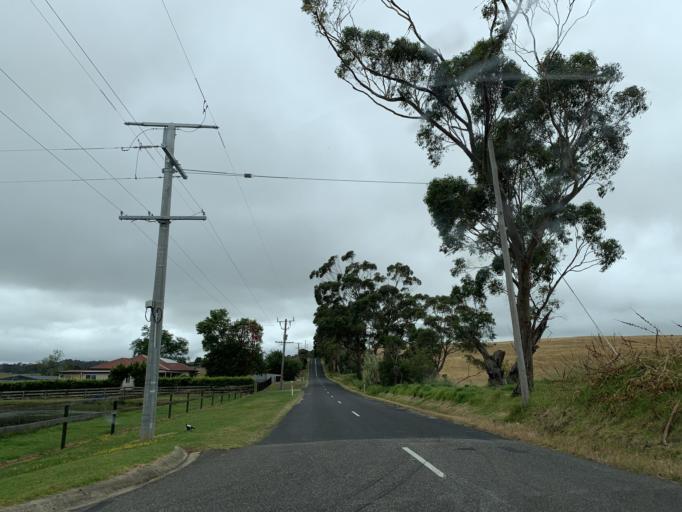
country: AU
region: Victoria
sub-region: Cardinia
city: Bunyip
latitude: -38.1781
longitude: 145.7654
